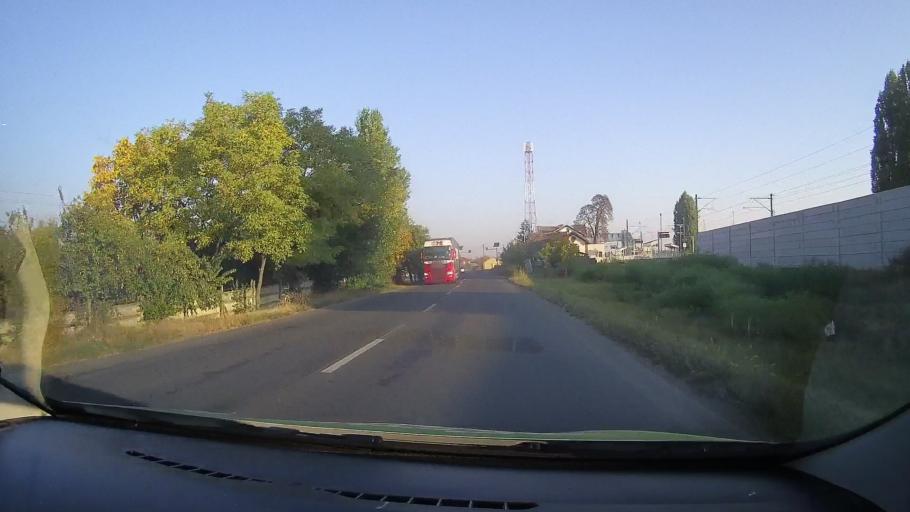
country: RO
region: Arad
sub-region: Comuna Sofronea
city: Sofronea
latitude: 46.2760
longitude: 21.3145
